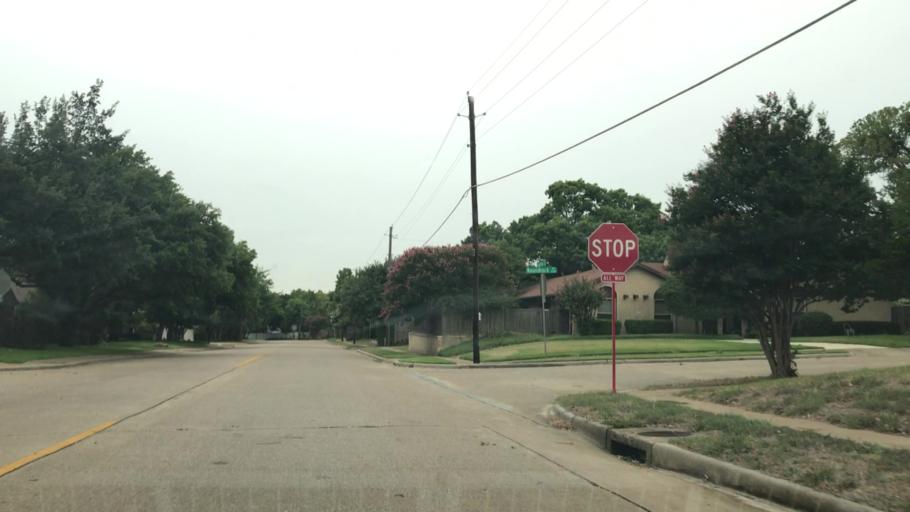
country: US
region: Texas
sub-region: Dallas County
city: Addison
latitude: 32.9569
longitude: -96.7920
